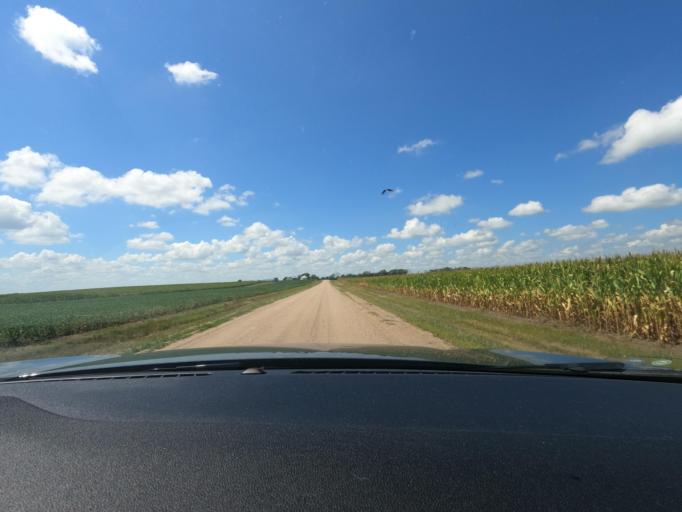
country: US
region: Nebraska
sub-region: Saunders County
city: Wahoo
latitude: 41.2493
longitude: -96.5531
